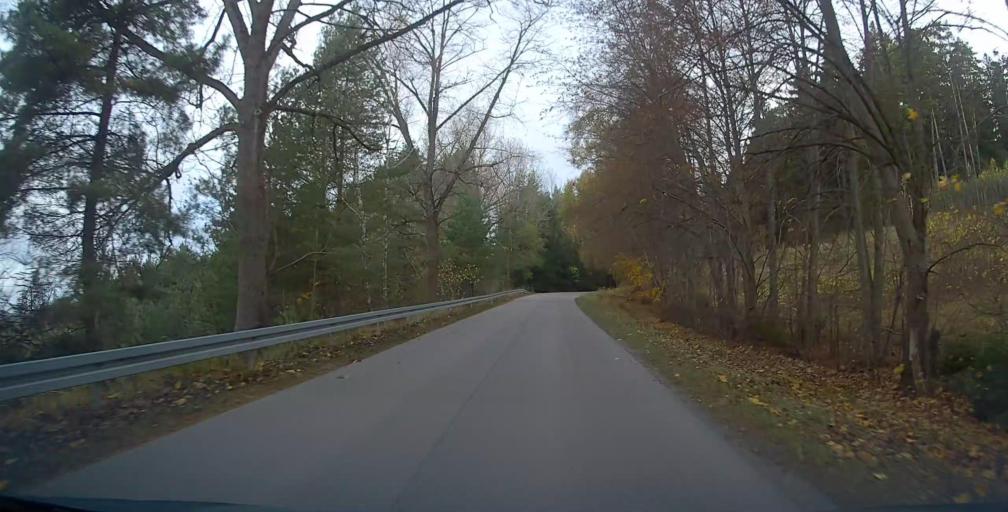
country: PL
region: Podlasie
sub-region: Suwalki
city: Suwalki
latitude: 54.2847
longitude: 22.8924
